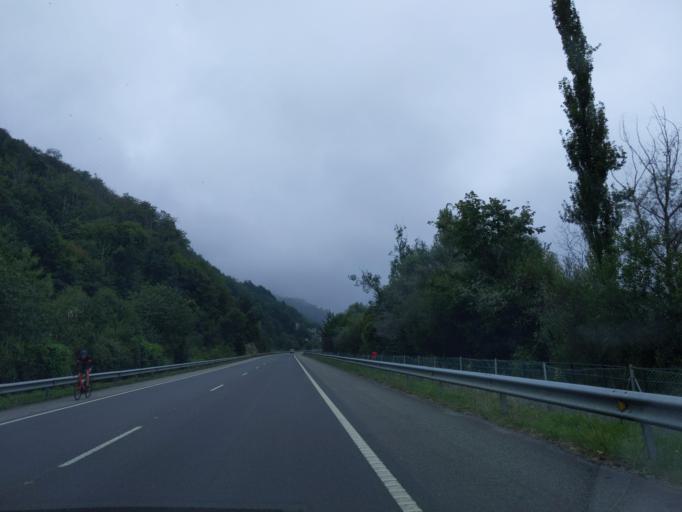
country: ES
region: Asturias
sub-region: Province of Asturias
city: Pola de Laviana
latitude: 43.2392
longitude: -5.5645
